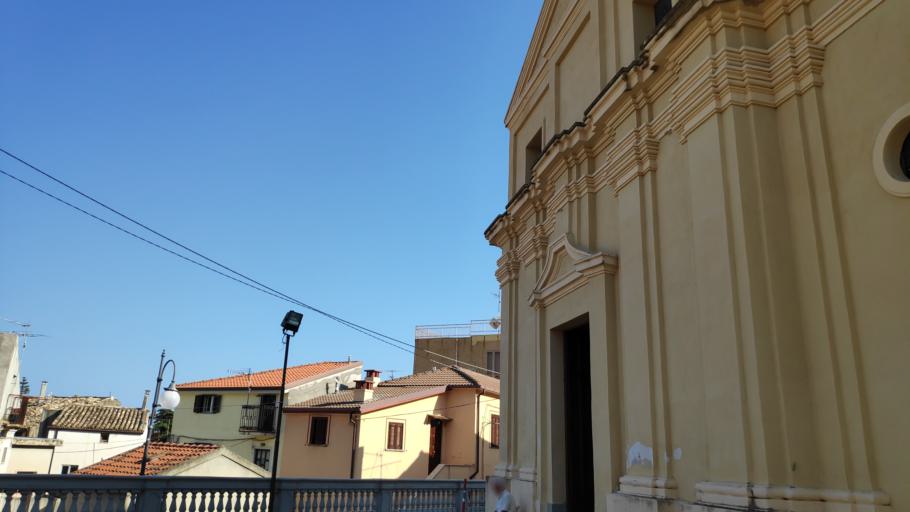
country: IT
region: Calabria
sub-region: Provincia di Catanzaro
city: Soverato Superiore
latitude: 38.6888
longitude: 16.5309
